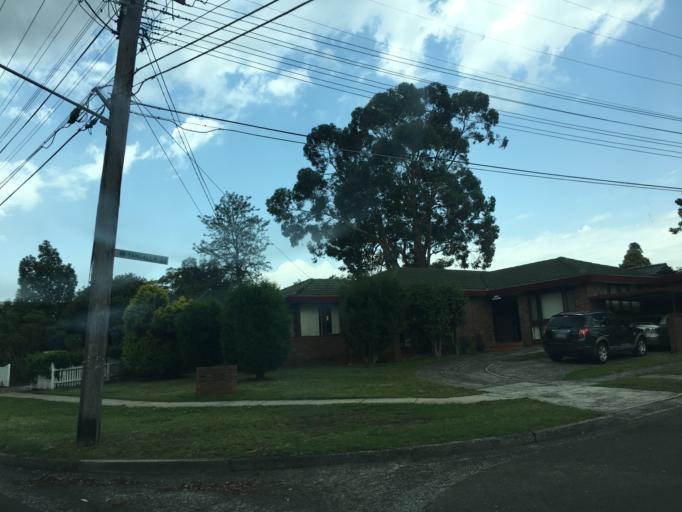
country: AU
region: New South Wales
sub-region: Ryde
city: Marsfield
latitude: -33.7751
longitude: 151.0986
